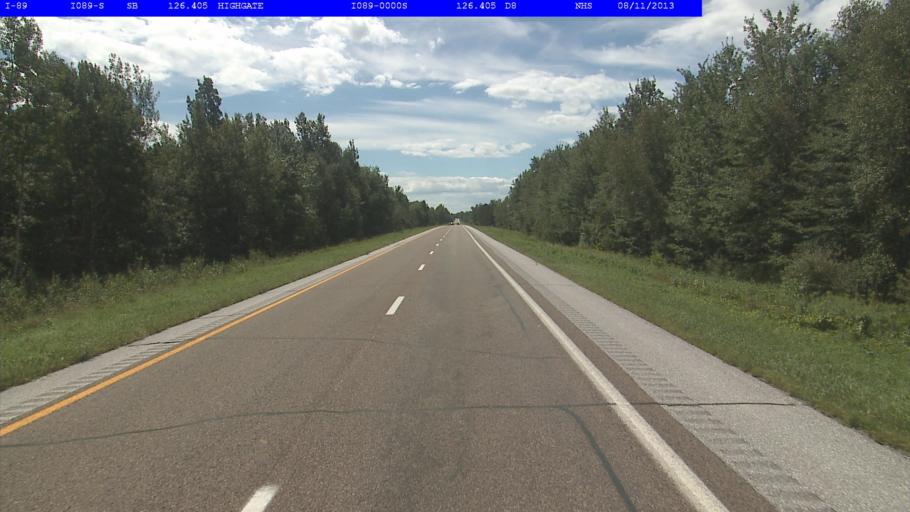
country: US
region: Vermont
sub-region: Franklin County
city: Swanton
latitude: 44.9648
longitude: -73.1073
